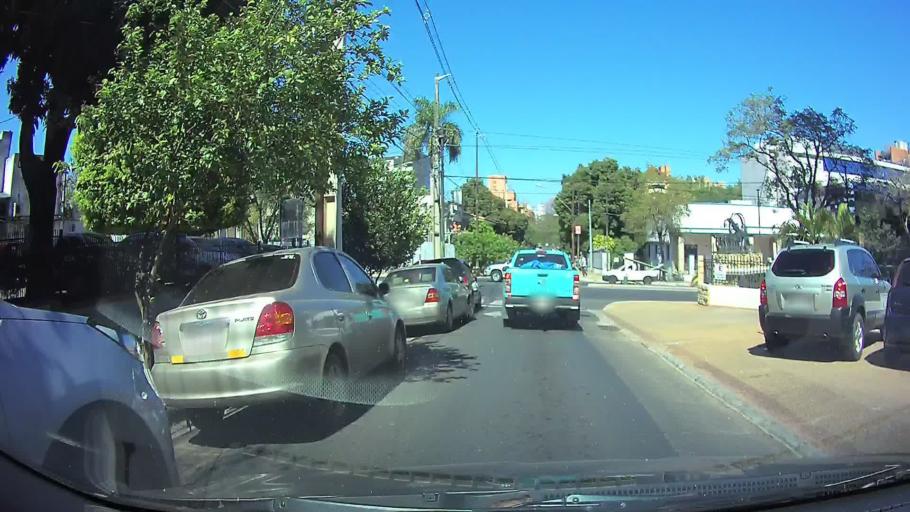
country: PY
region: Asuncion
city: Asuncion
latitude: -25.2917
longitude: -57.6145
